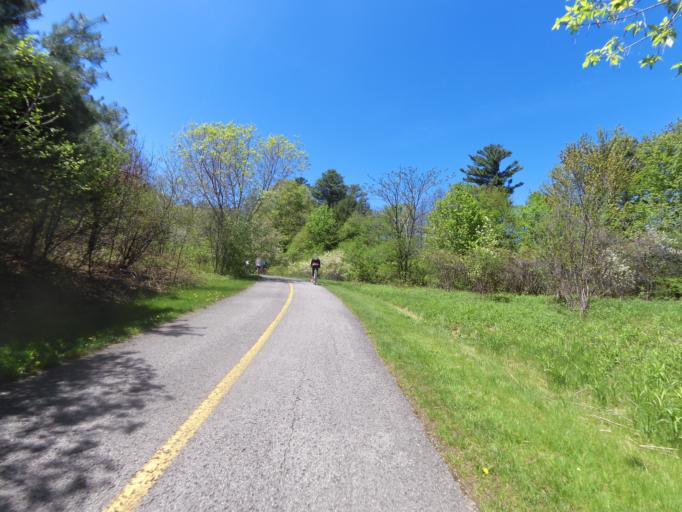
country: CA
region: Ontario
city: Ottawa
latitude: 45.4310
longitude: -75.7700
